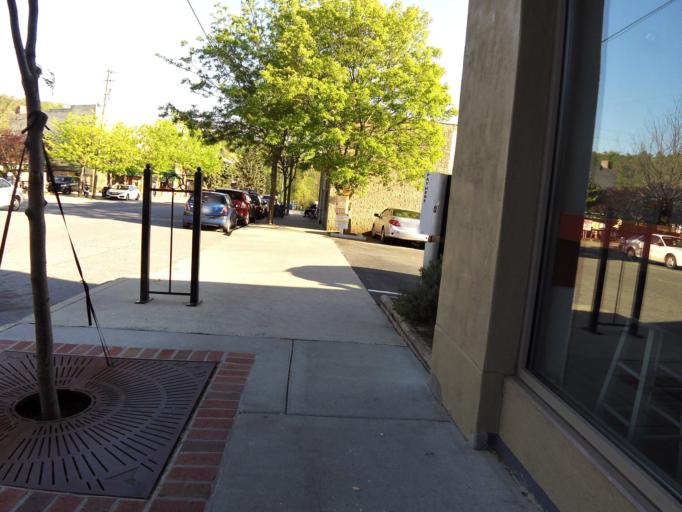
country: US
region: North Carolina
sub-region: Buncombe County
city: Asheville
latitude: 35.5923
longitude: -82.5510
